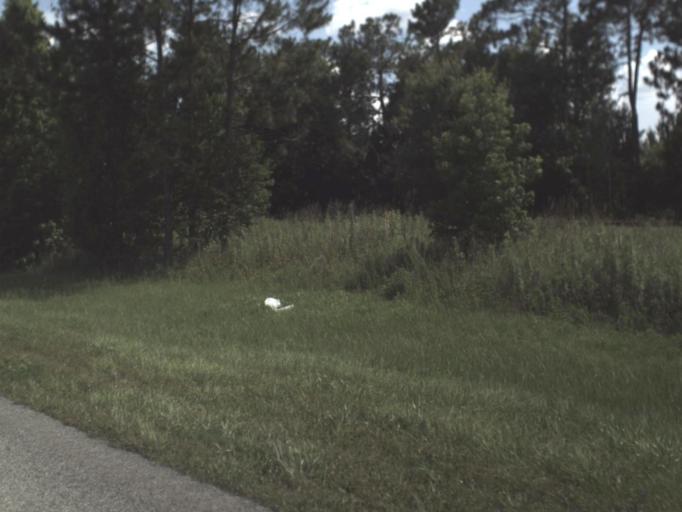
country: US
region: Florida
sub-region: Alachua County
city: Hawthorne
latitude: 29.6757
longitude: -82.1219
